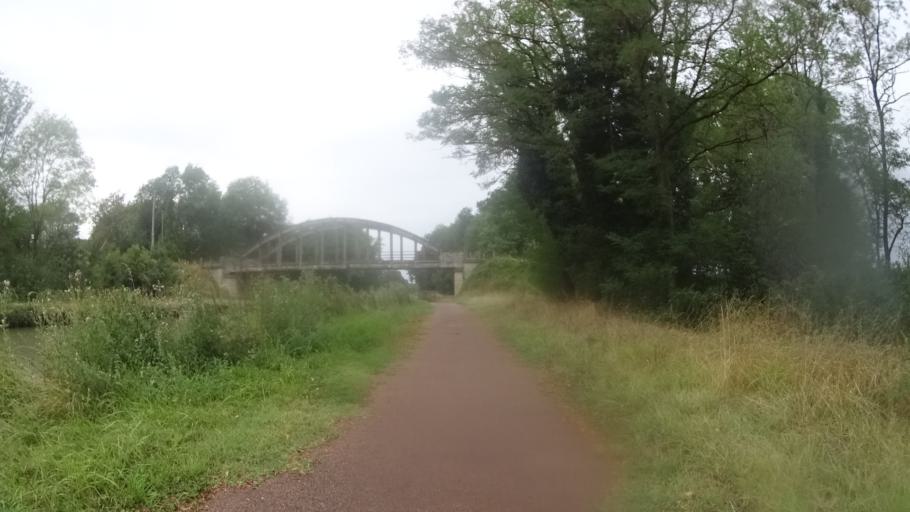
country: FR
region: Bourgogne
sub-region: Departement de la Nievre
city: Imphy
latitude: 46.8663
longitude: 3.2809
